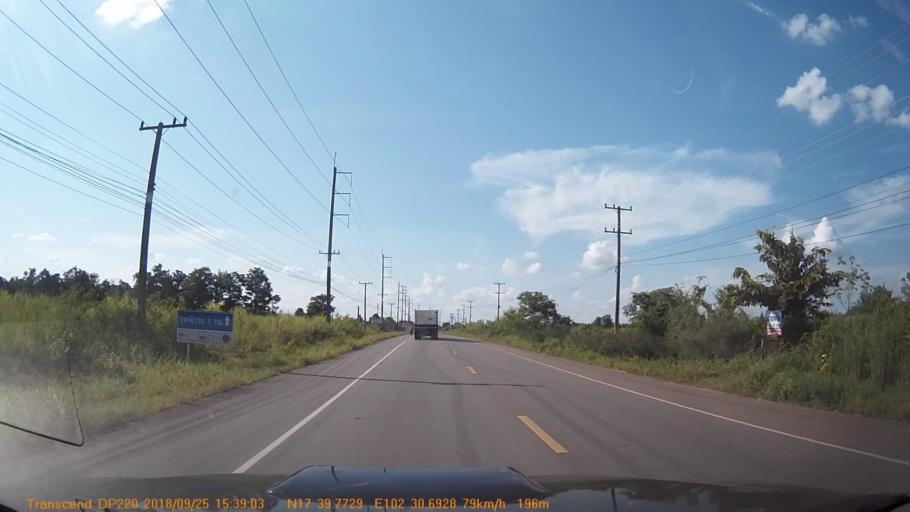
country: TH
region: Changwat Udon Thani
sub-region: Amphoe Ban Phue
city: Ban Phue
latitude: 17.6632
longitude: 102.5114
